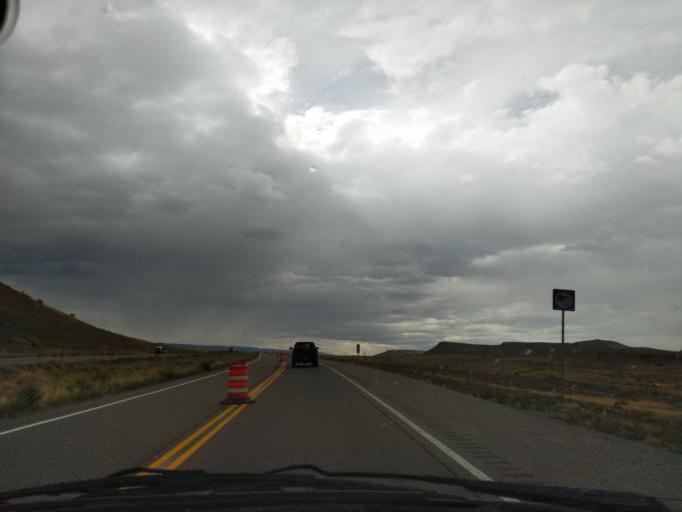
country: US
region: Colorado
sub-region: Delta County
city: Delta
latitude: 38.7549
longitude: -108.1721
